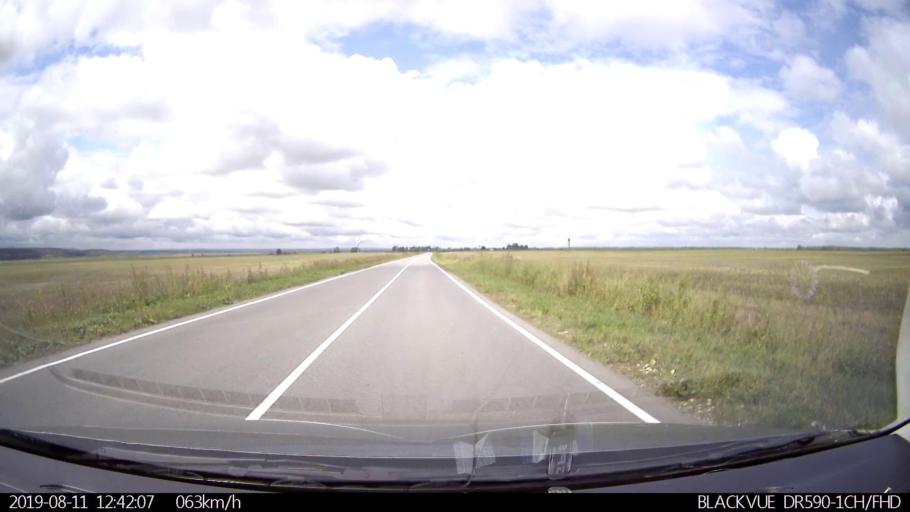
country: RU
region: Ulyanovsk
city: Ignatovka
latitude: 53.8434
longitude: 47.7553
